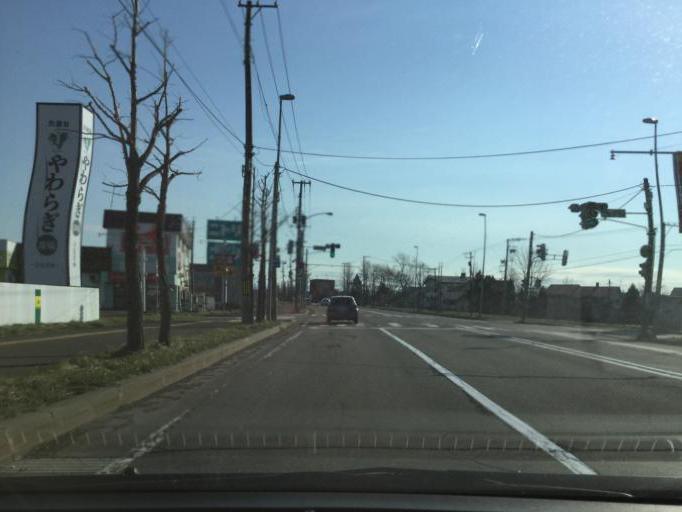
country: JP
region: Hokkaido
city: Iwamizawa
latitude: 43.1893
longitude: 141.7546
